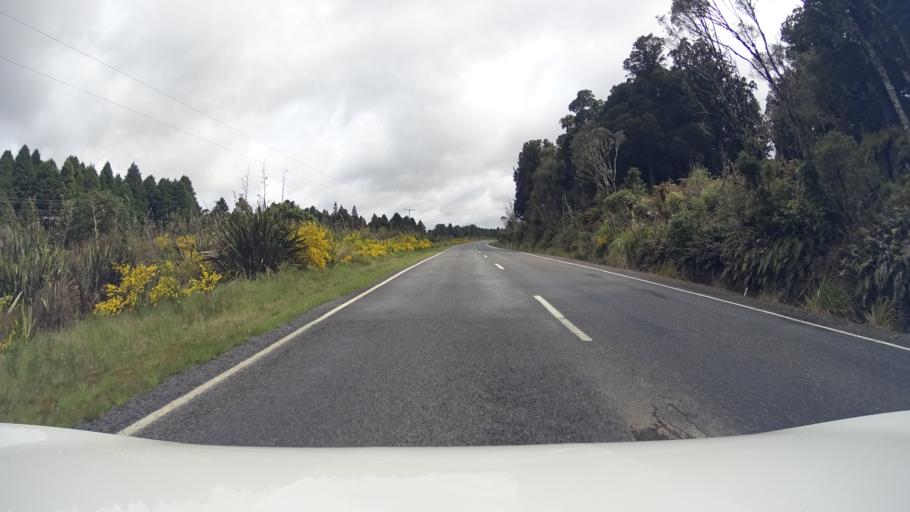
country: NZ
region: Manawatu-Wanganui
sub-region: Ruapehu District
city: Waiouru
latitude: -39.2492
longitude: 175.3886
